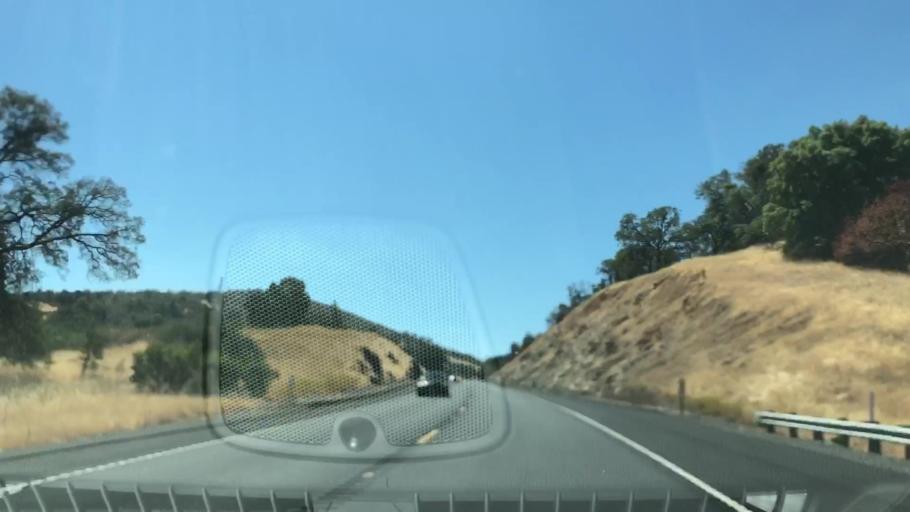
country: US
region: California
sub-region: Calaveras County
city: Copperopolis
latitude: 37.9527
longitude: -120.6950
